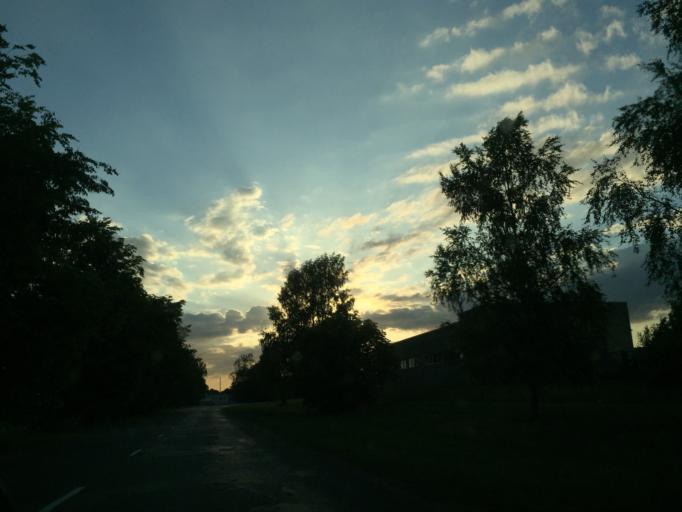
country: LV
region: Sigulda
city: Sigulda
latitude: 57.1411
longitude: 24.8635
